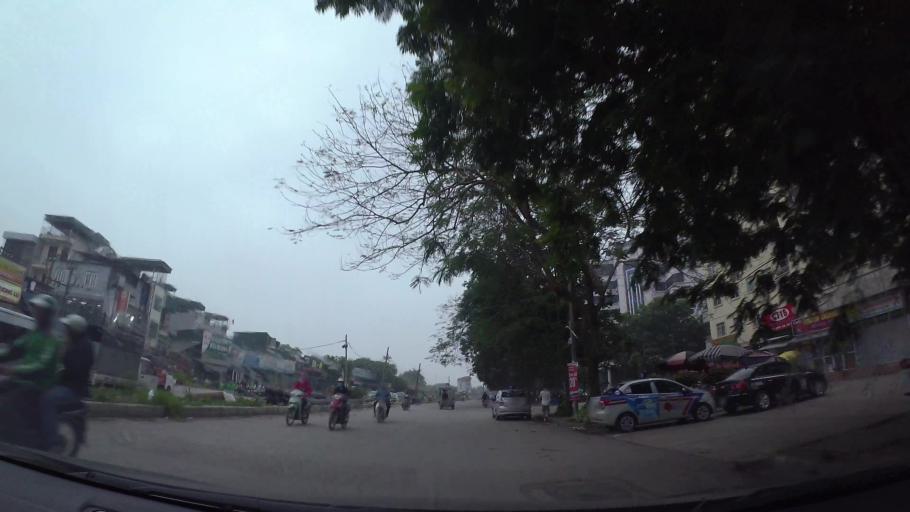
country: VN
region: Ha Noi
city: Thanh Xuan
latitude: 20.9840
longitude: 105.8307
